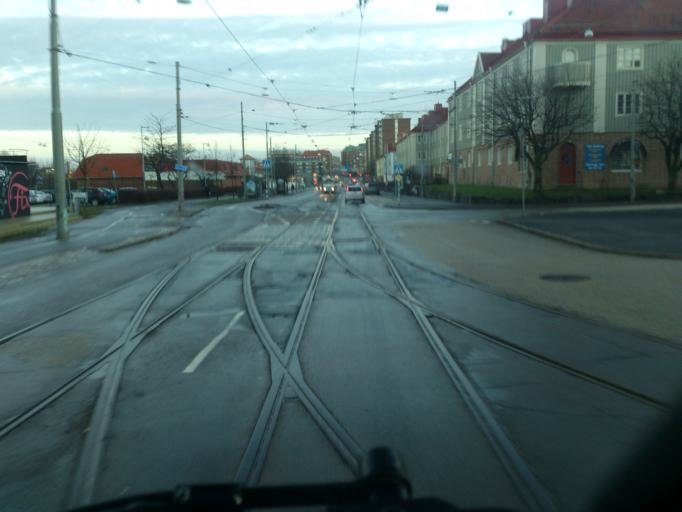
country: SE
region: Vaestra Goetaland
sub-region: Goteborg
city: Majorna
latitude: 57.6893
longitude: 11.9115
